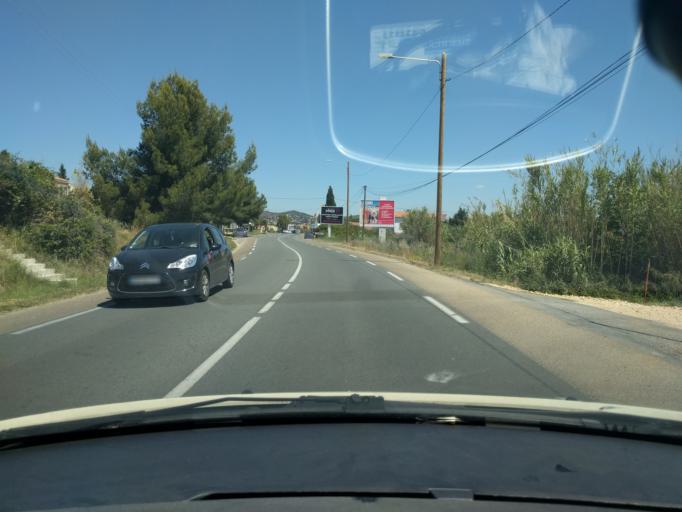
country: FR
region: Provence-Alpes-Cote d'Azur
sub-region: Departement du Var
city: Hyeres
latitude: 43.0958
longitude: 6.1315
